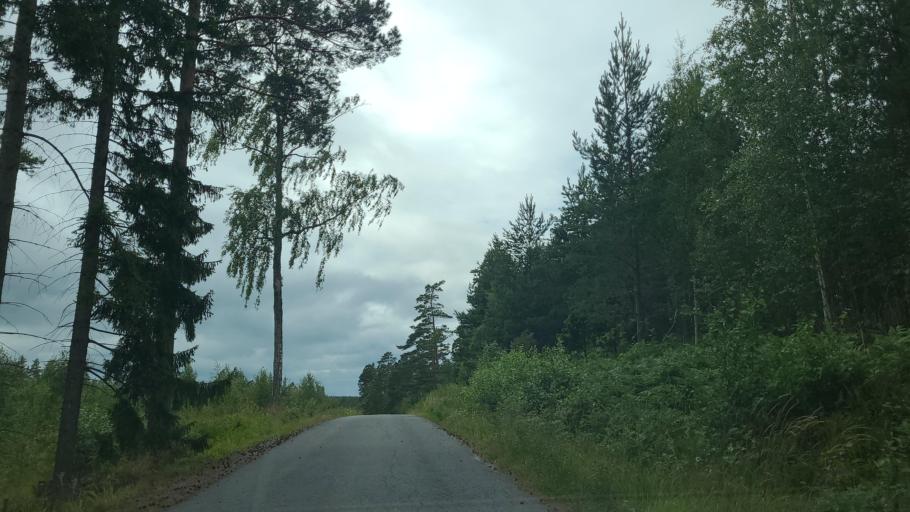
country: FI
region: Varsinais-Suomi
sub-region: Aboland-Turunmaa
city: Dragsfjaerd
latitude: 60.0973
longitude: 22.4293
